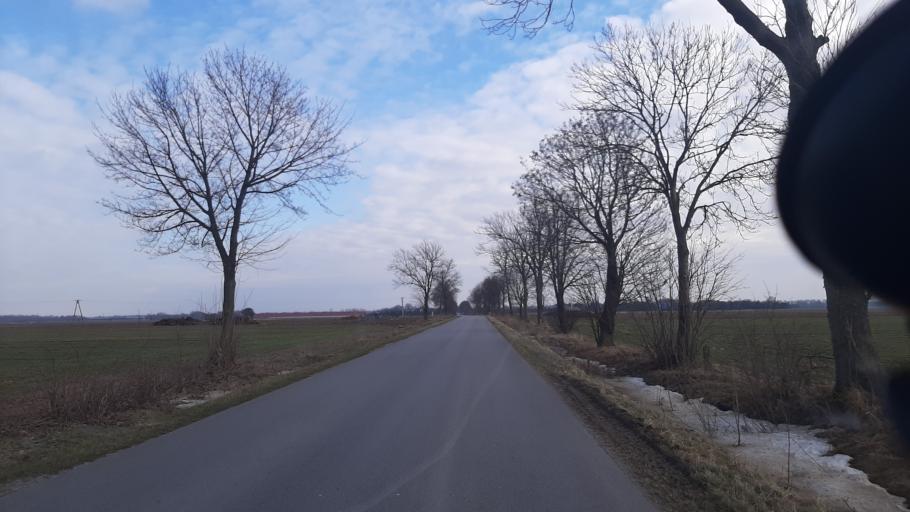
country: PL
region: Lublin Voivodeship
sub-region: Powiat lubartowski
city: Ostrow Lubelski
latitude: 51.4821
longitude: 22.8962
